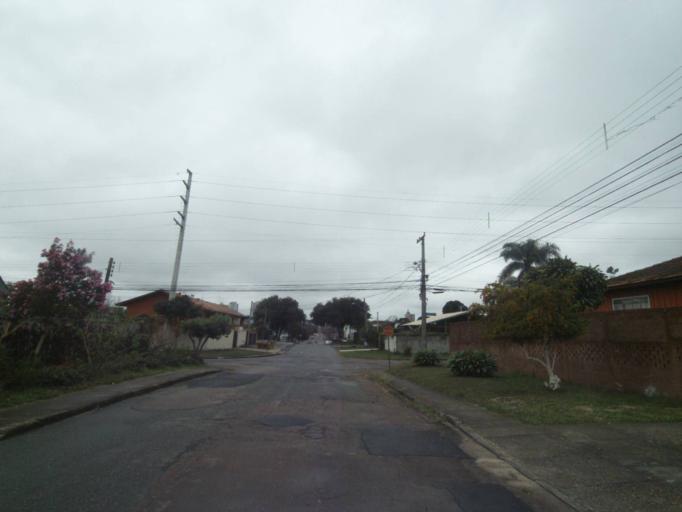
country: BR
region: Parana
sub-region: Curitiba
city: Curitiba
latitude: -25.5154
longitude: -49.3065
